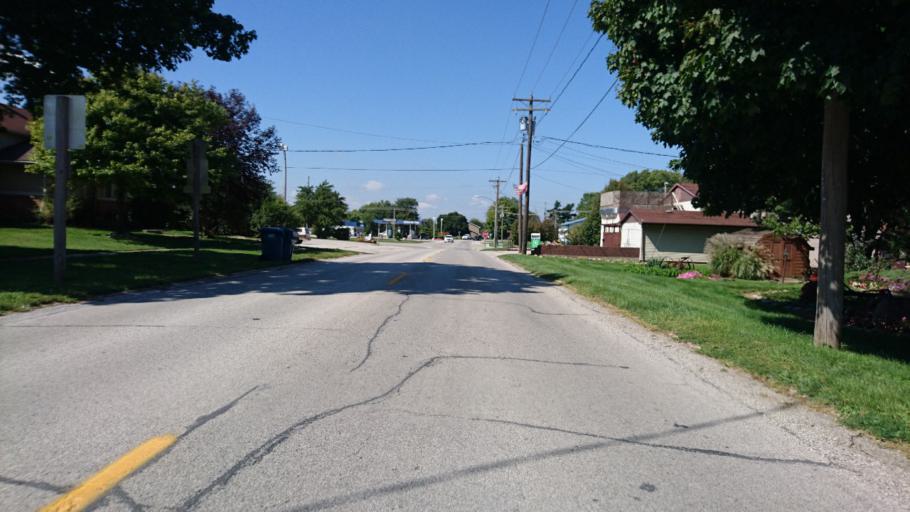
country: US
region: Illinois
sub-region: McLean County
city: Lexington
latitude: 40.6415
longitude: -88.7906
